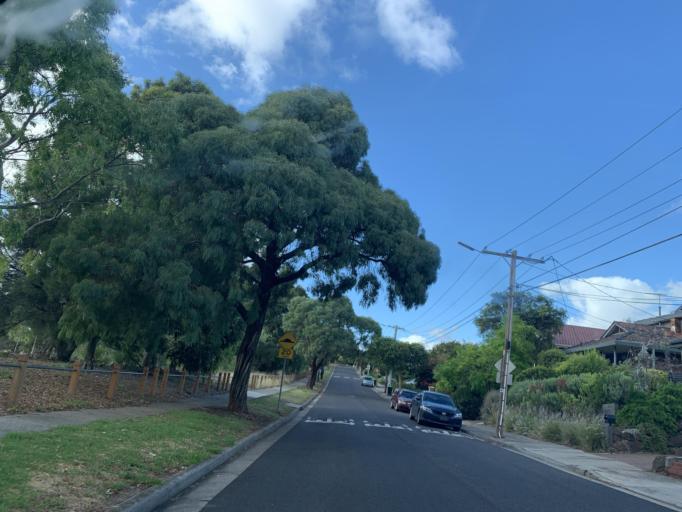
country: AU
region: Victoria
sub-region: Moreland
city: Gowanbrae
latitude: -37.7147
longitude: 144.8979
